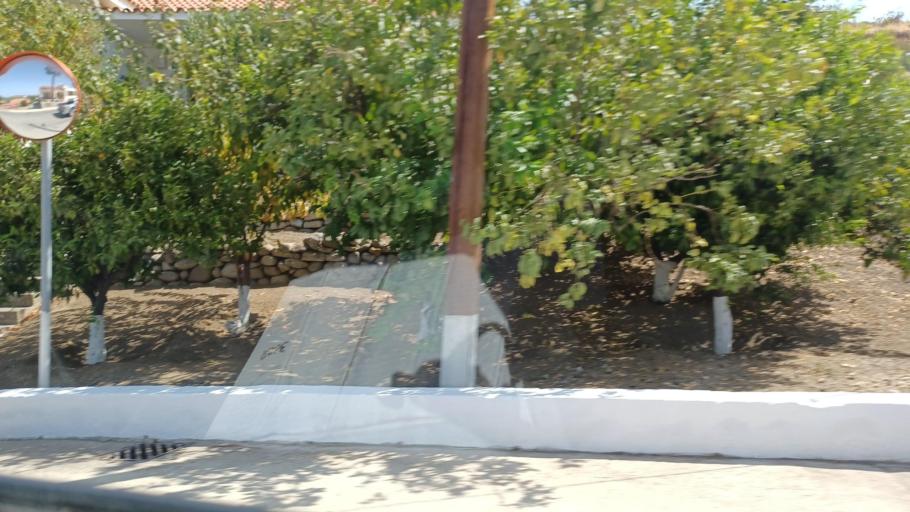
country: CY
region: Lefkosia
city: Lefka
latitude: 35.0751
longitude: 32.8949
